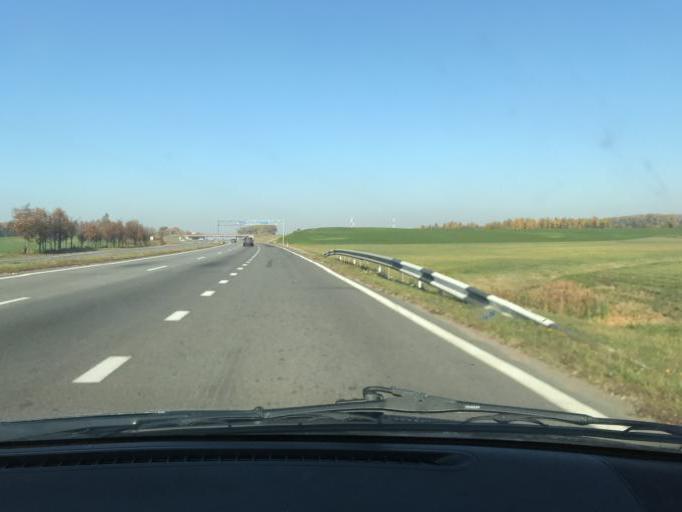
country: BY
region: Minsk
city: Samakhvalavichy
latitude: 53.7205
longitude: 27.5188
